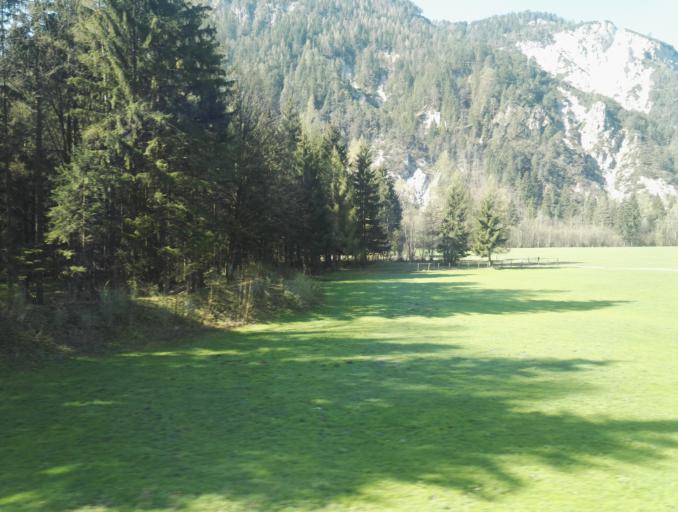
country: AT
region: Salzburg
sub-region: Politischer Bezirk Sankt Johann im Pongau
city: Forstau
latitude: 47.3992
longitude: 13.5881
